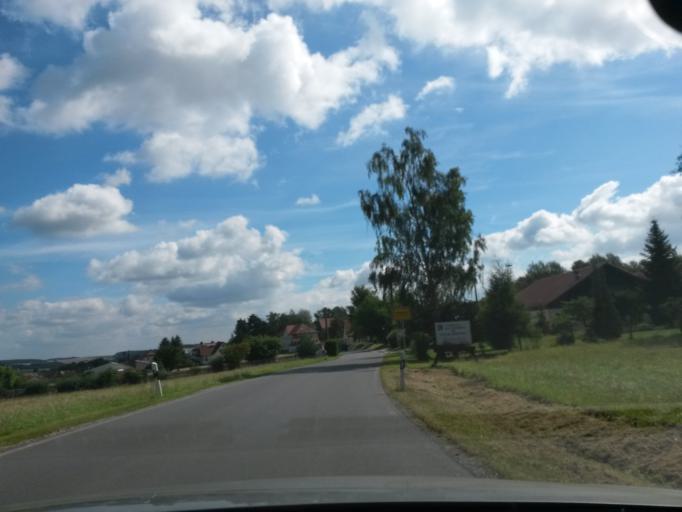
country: DE
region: Thuringia
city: Reichenbach
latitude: 50.8634
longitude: 11.8682
